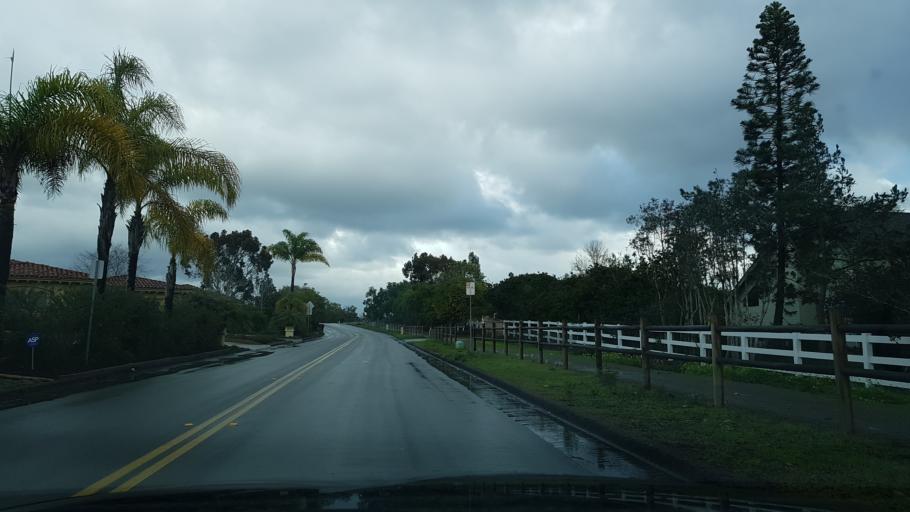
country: US
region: California
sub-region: San Diego County
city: Fairbanks Ranch
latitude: 32.9418
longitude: -117.2058
